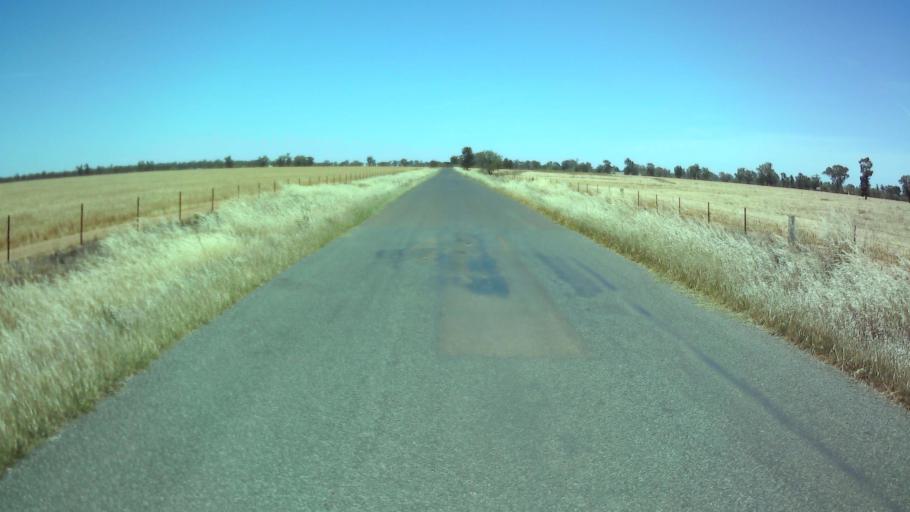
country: AU
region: New South Wales
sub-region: Weddin
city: Grenfell
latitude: -34.0501
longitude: 147.7818
